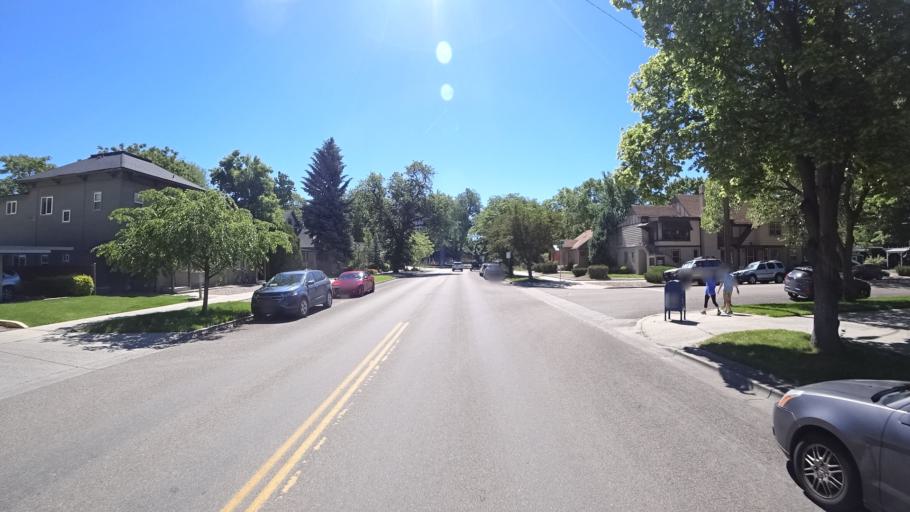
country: US
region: Idaho
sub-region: Ada County
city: Boise
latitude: 43.6212
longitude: -116.1966
